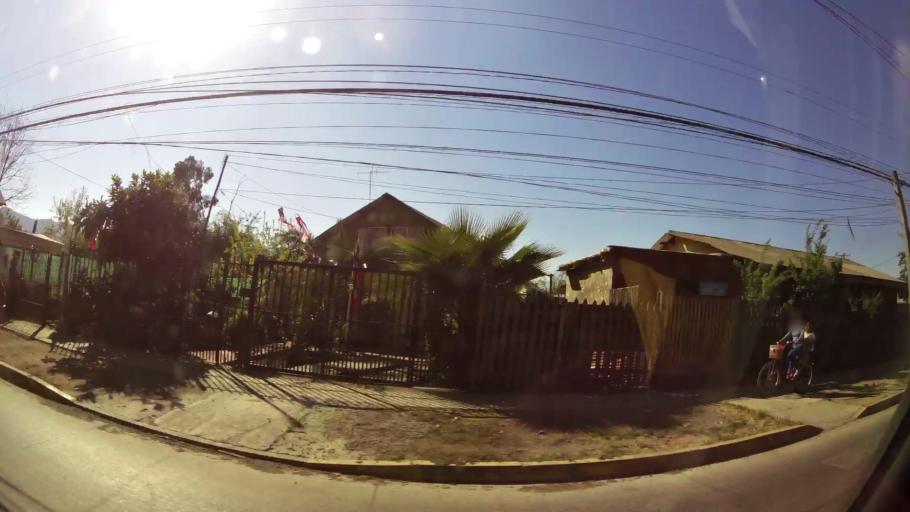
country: CL
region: Santiago Metropolitan
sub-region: Provincia de Talagante
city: Penaflor
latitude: -33.6050
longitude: -70.8893
